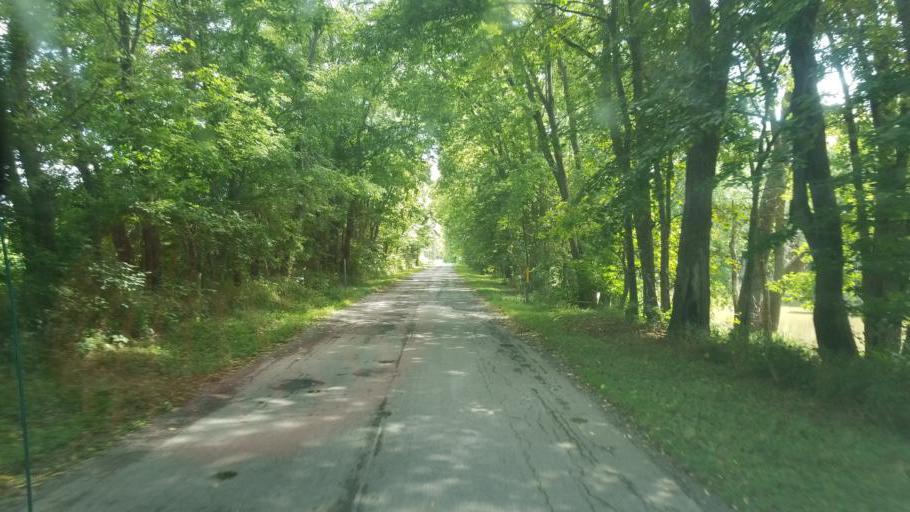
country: US
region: Ohio
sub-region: Marion County
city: Prospect
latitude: 40.4304
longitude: -83.1927
